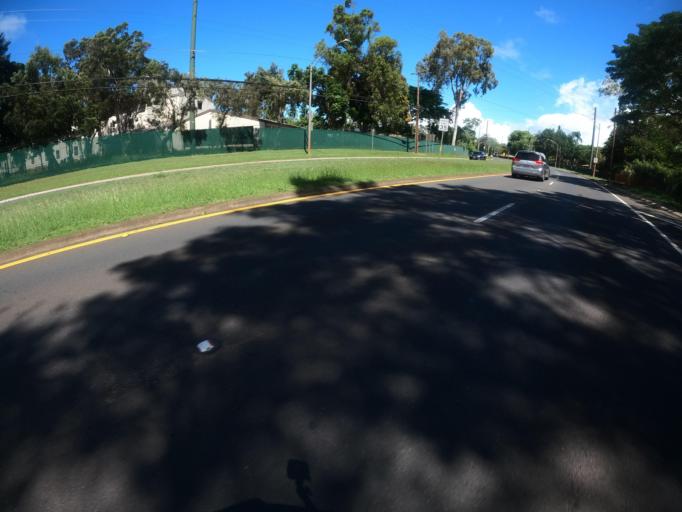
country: US
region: Hawaii
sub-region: Honolulu County
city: Schofield Barracks
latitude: 21.4851
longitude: -158.0436
